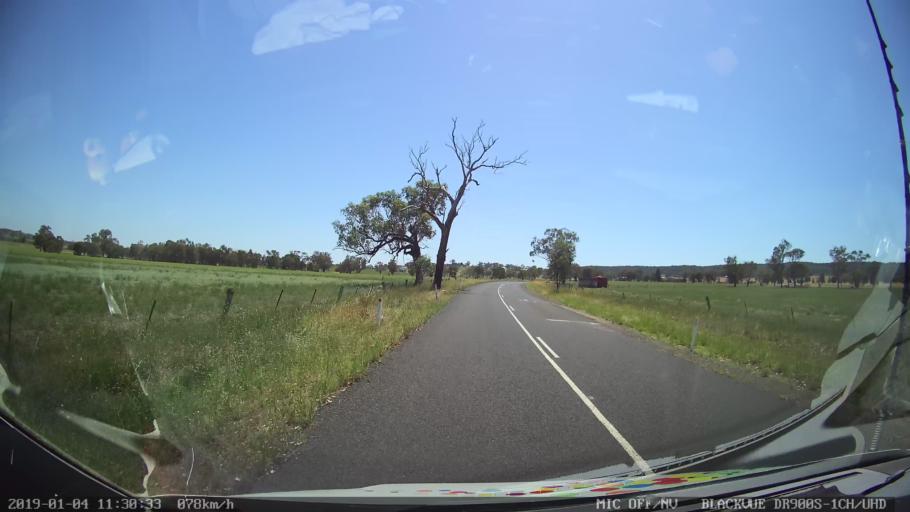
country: AU
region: New South Wales
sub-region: Cabonne
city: Molong
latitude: -33.0769
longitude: 148.7823
